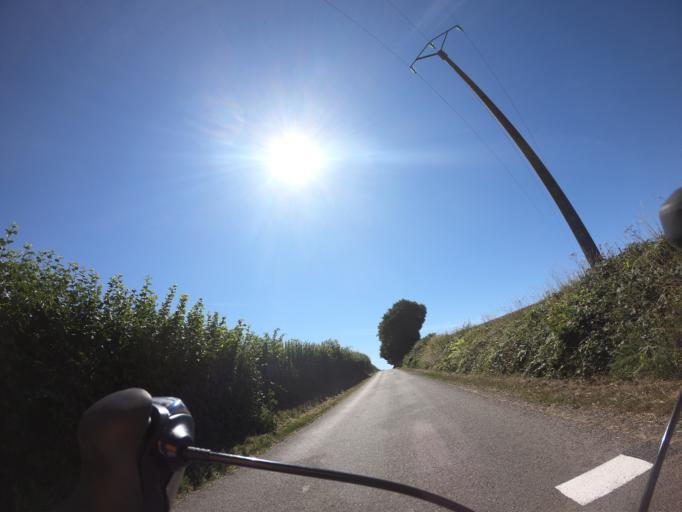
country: FR
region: Lower Normandy
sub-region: Departement de l'Orne
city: Saint-Denis-sur-Sarthon
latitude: 48.5252
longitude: -0.0899
